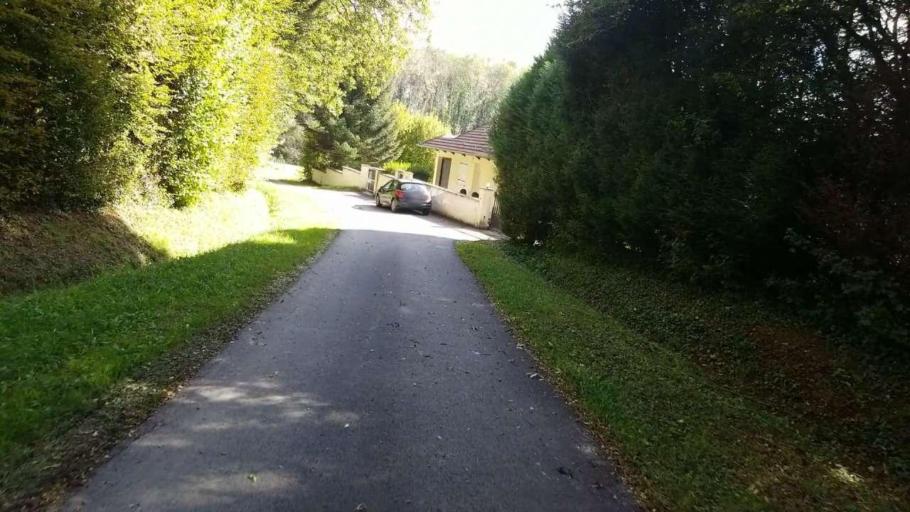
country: FR
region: Franche-Comte
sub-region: Departement du Jura
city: Bletterans
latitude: 46.8319
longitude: 5.4653
